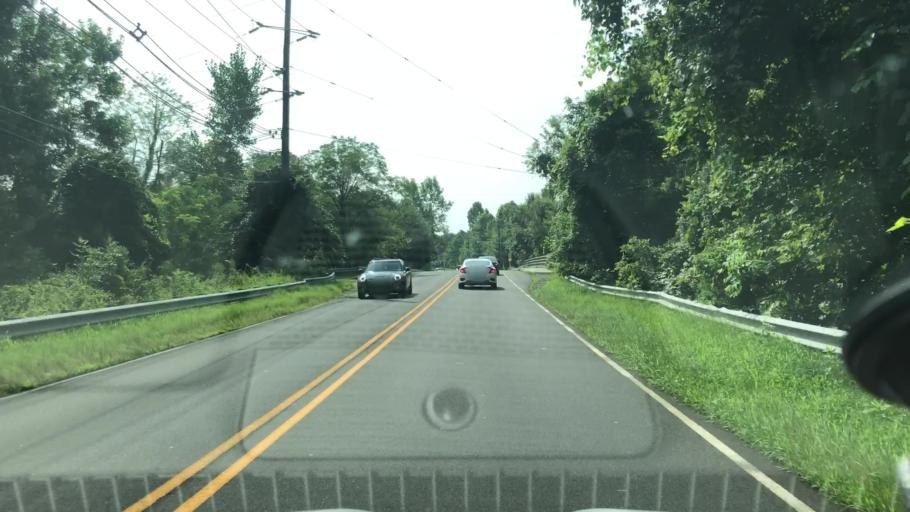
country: US
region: New Jersey
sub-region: Mercer County
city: Lawrenceville
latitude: 40.3030
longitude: -74.6890
